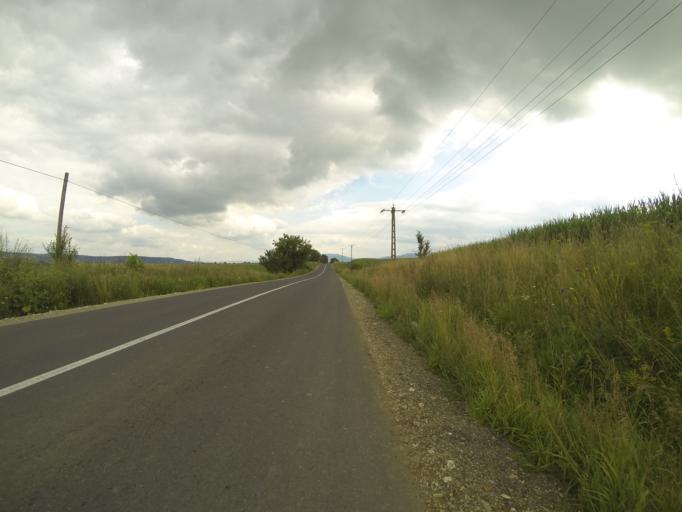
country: RO
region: Brasov
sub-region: Comuna Parau
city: Parau
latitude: 45.8392
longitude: 25.1646
